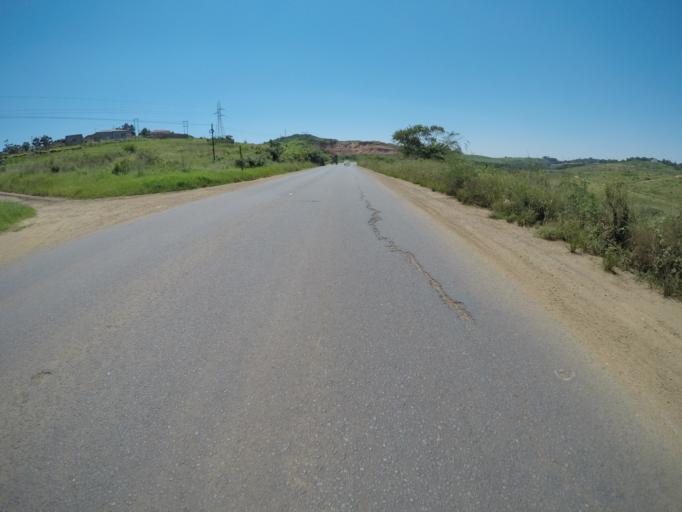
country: ZA
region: KwaZulu-Natal
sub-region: uThungulu District Municipality
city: Empangeni
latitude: -28.7586
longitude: 31.8743
